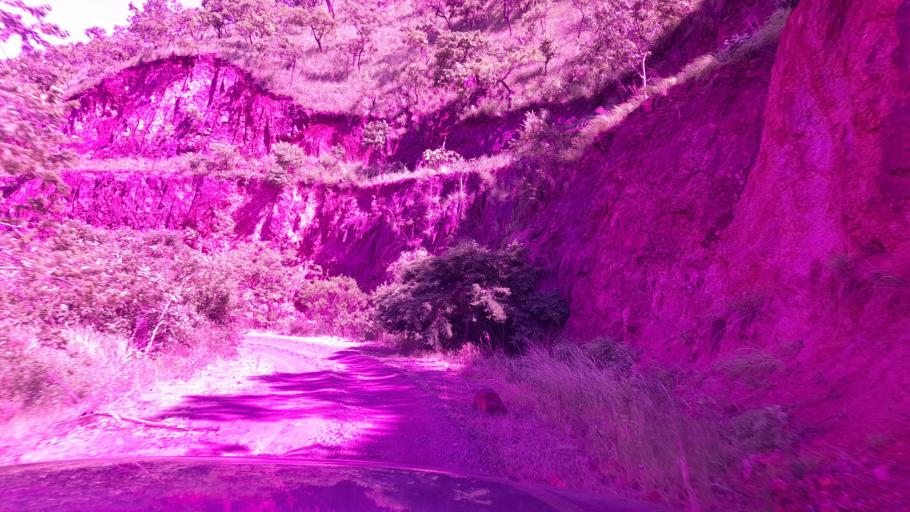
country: ET
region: Southern Nations, Nationalities, and People's Region
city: K'olito
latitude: 7.7809
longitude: 37.5573
